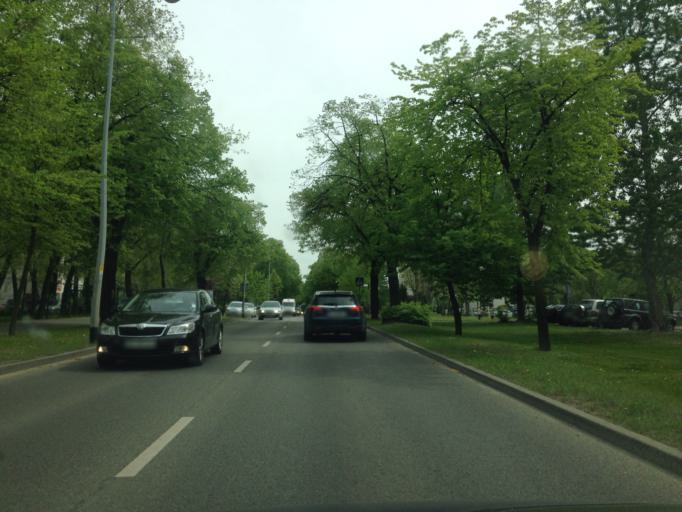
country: PL
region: Pomeranian Voivodeship
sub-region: Sopot
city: Sopot
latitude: 54.4234
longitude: 18.5788
